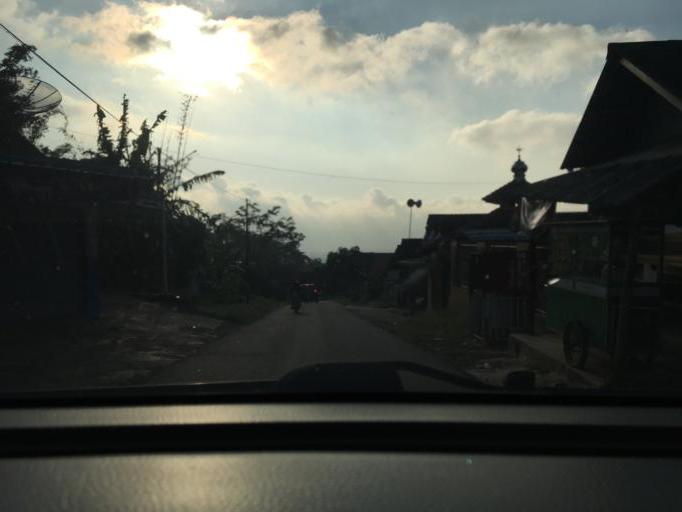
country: ID
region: West Java
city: Nagarakembang
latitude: -7.0361
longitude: 108.3263
